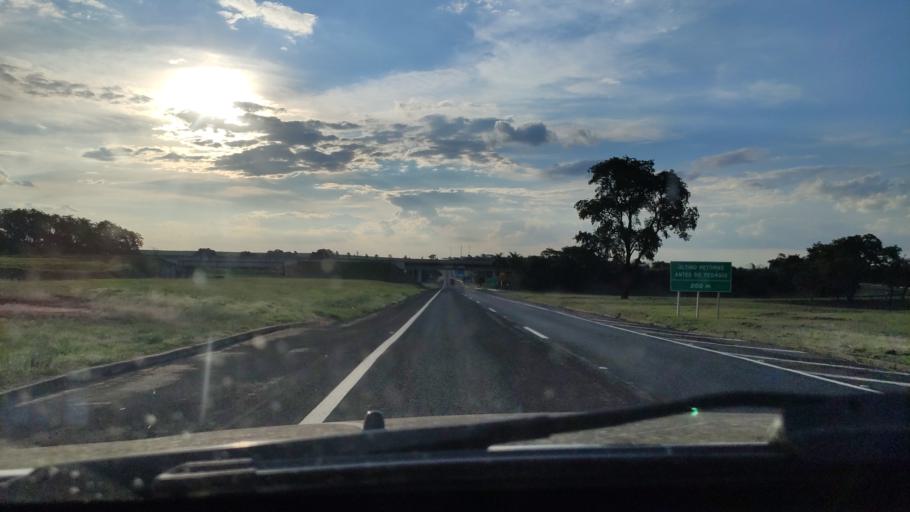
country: BR
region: Sao Paulo
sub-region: Rancharia
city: Rancharia
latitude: -22.4426
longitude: -50.9958
